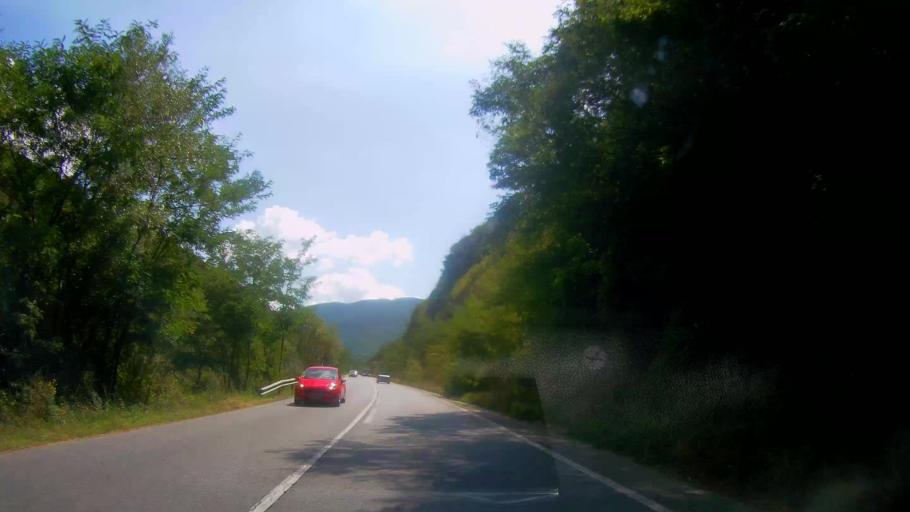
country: BG
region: Stara Zagora
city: Gurkovo
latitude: 42.7252
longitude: 25.7127
